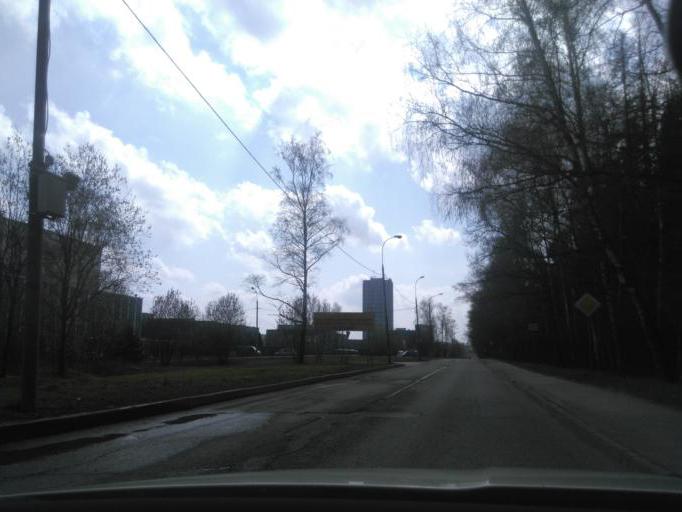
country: RU
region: Moskovskaya
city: Mendeleyevo
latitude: 56.0183
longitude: 37.1951
